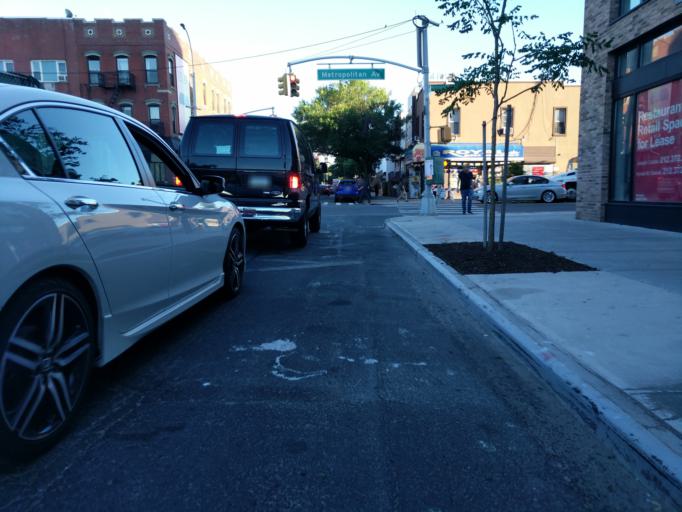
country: US
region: New York
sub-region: Queens County
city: Long Island City
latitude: 40.7149
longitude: -73.9428
